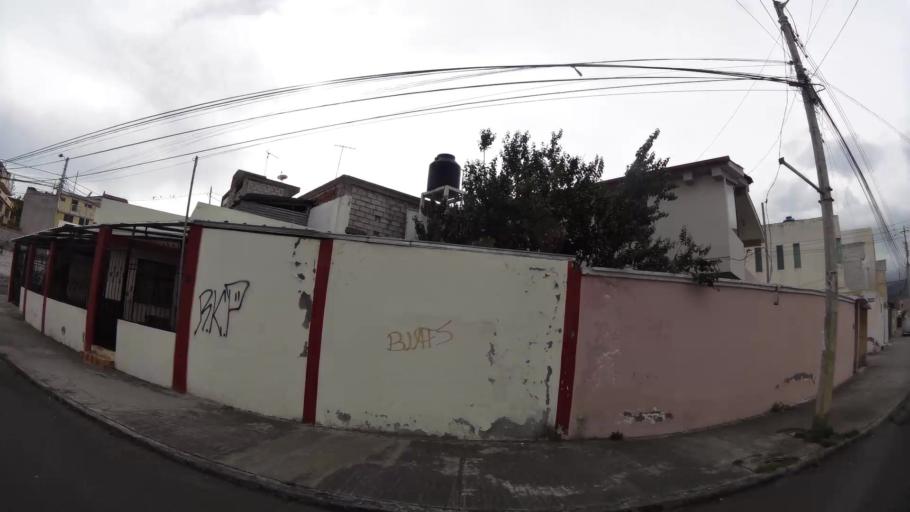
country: EC
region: Tungurahua
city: Ambato
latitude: -1.2626
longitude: -78.6319
